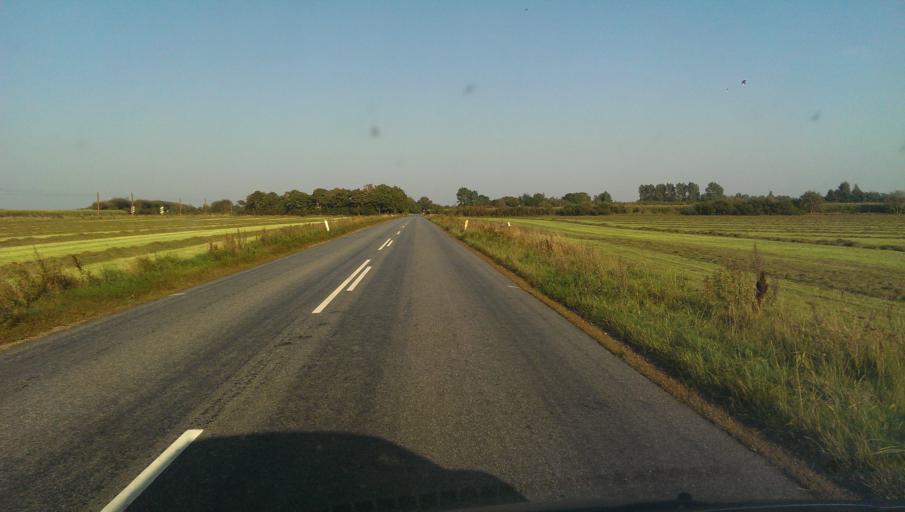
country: DK
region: South Denmark
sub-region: Esbjerg Kommune
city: Bramming
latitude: 55.4649
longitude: 8.7256
